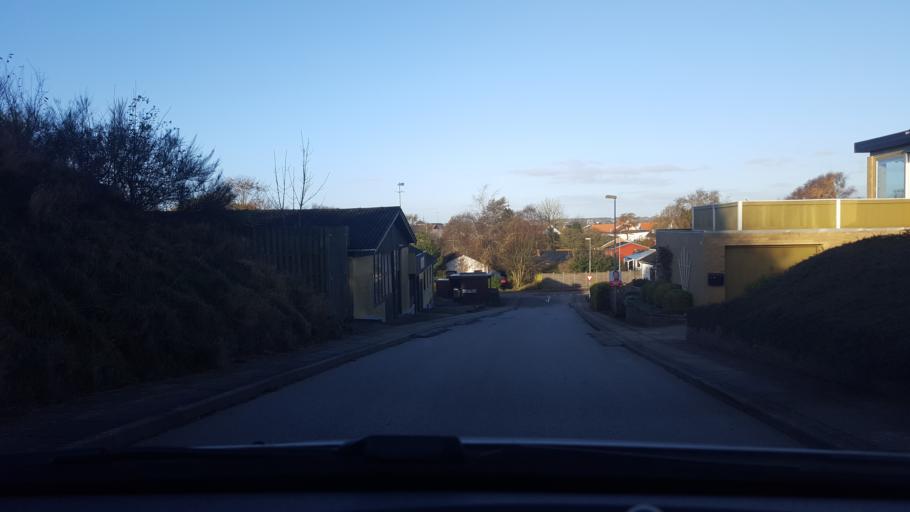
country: DK
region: North Denmark
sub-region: Morso Kommune
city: Nykobing Mors
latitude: 56.7600
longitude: 8.8772
